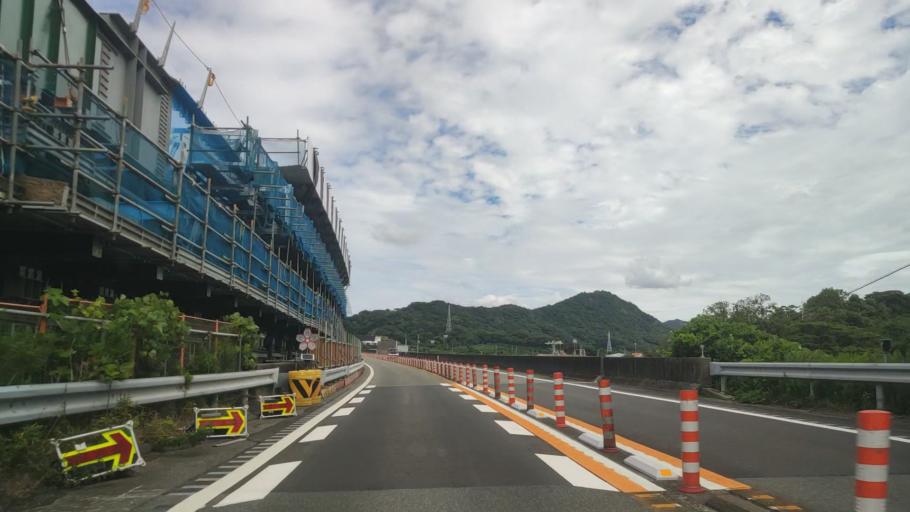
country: JP
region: Wakayama
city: Gobo
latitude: 33.9056
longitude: 135.1921
